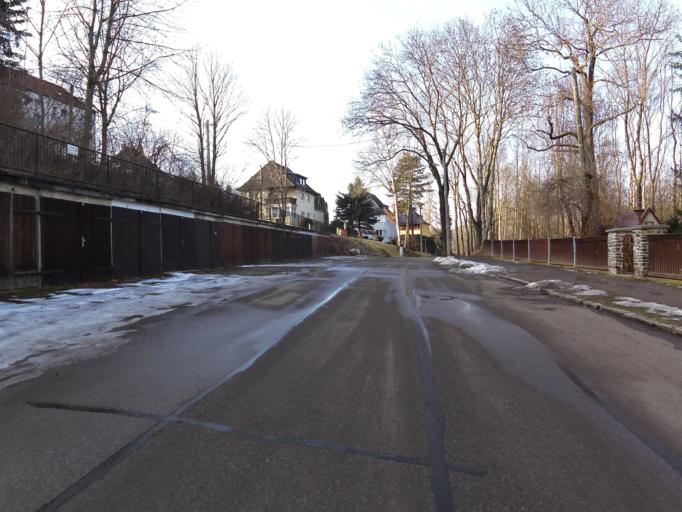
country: DE
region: Saxony
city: Glauchau
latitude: 50.8237
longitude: 12.5583
